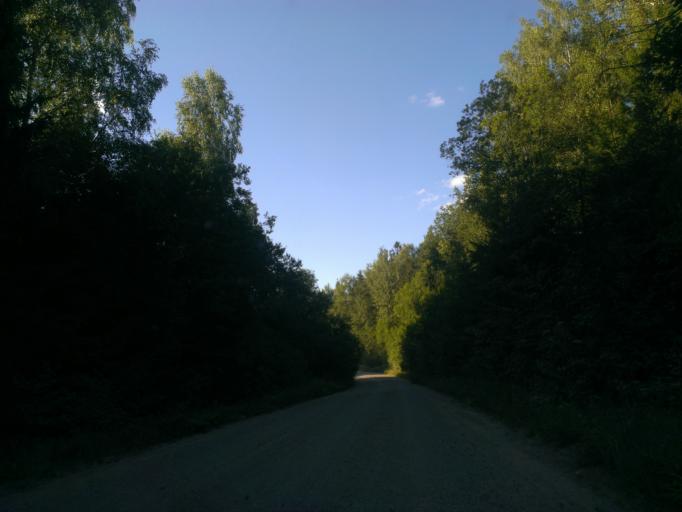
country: LV
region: Malpils
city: Malpils
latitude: 57.0955
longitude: 25.0474
